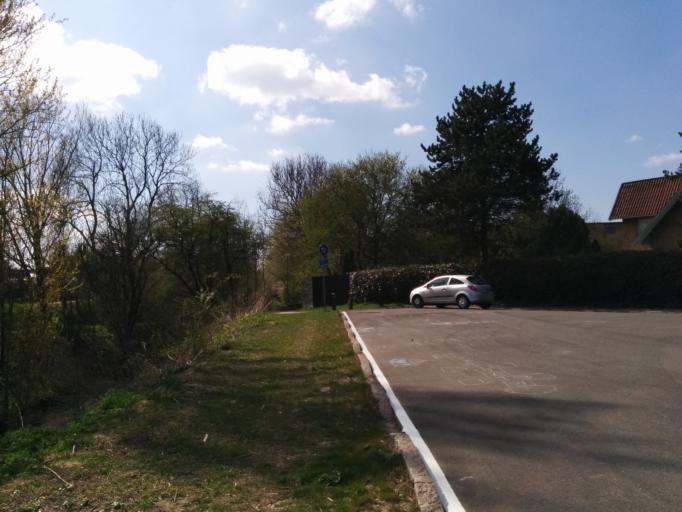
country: DK
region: Capital Region
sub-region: Frederiksberg Kommune
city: Frederiksberg
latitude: 55.7270
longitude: 12.5278
